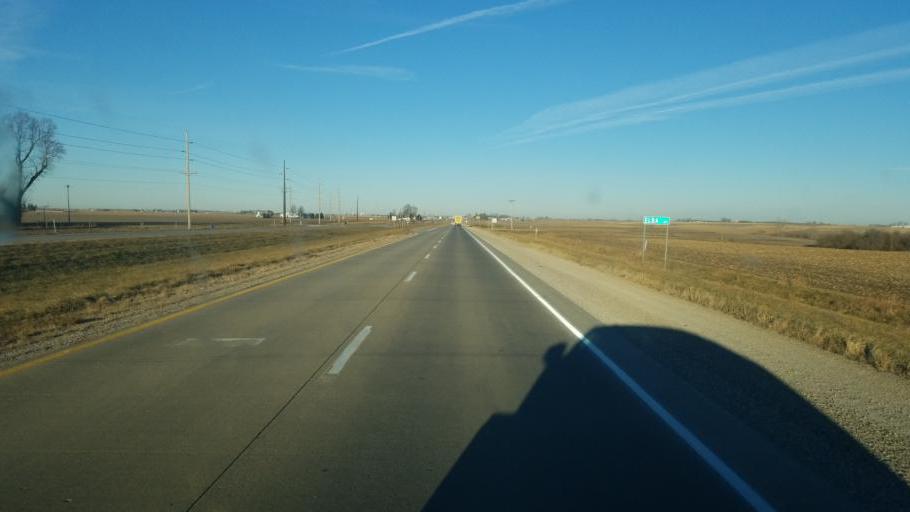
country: US
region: Iowa
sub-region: Mahaska County
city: Oskaloosa
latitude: 41.3590
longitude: -92.7730
